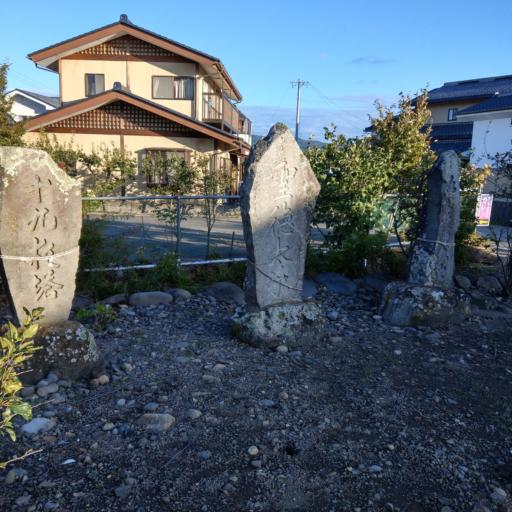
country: JP
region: Nagano
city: Saku
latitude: 36.2415
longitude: 138.4713
